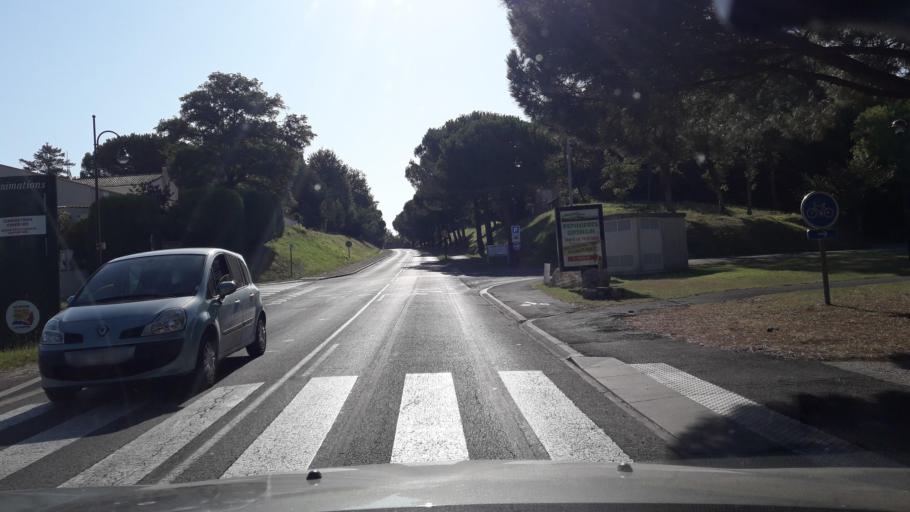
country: FR
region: Poitou-Charentes
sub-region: Departement de la Charente-Maritime
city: Les Mathes
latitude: 45.7153
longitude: -1.1479
